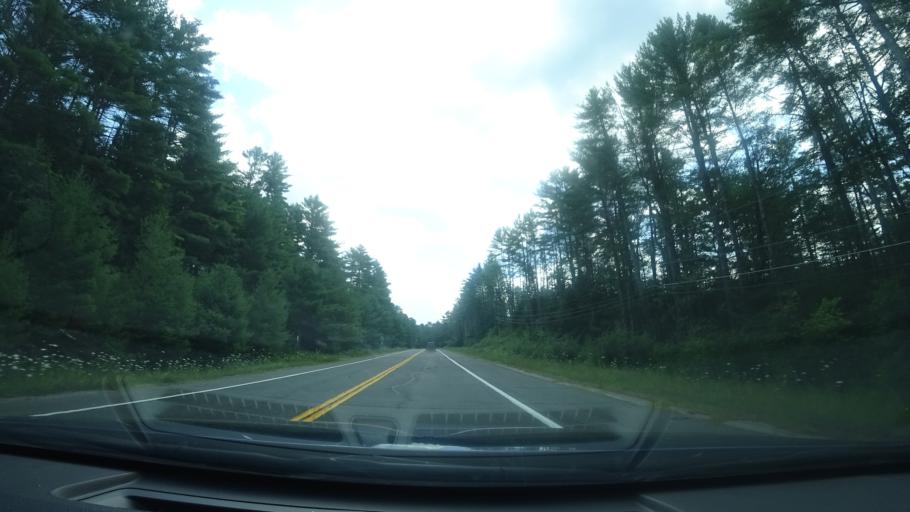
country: US
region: New York
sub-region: Warren County
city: Warrensburg
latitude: 43.6592
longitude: -73.8164
